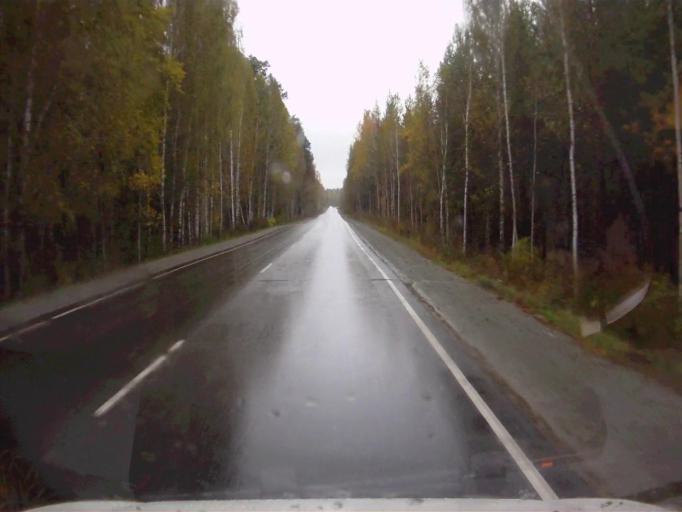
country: RU
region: Chelyabinsk
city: Kyshtym
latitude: 55.6484
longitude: 60.5826
